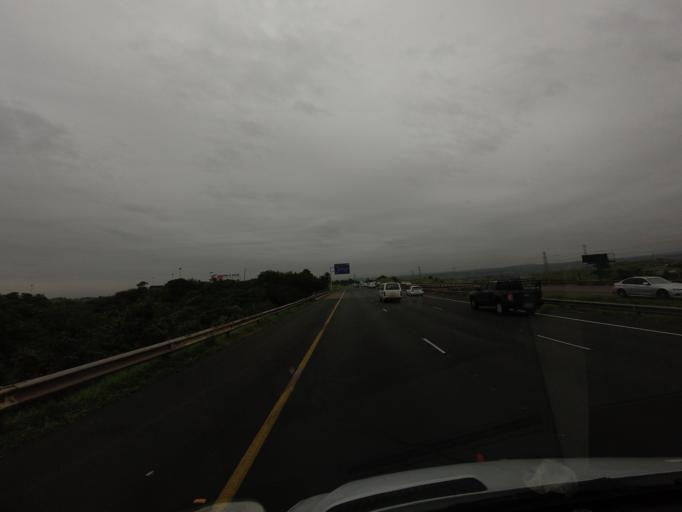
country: ZA
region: KwaZulu-Natal
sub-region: eThekwini Metropolitan Municipality
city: Durban
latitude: -29.7484
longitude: 31.0331
